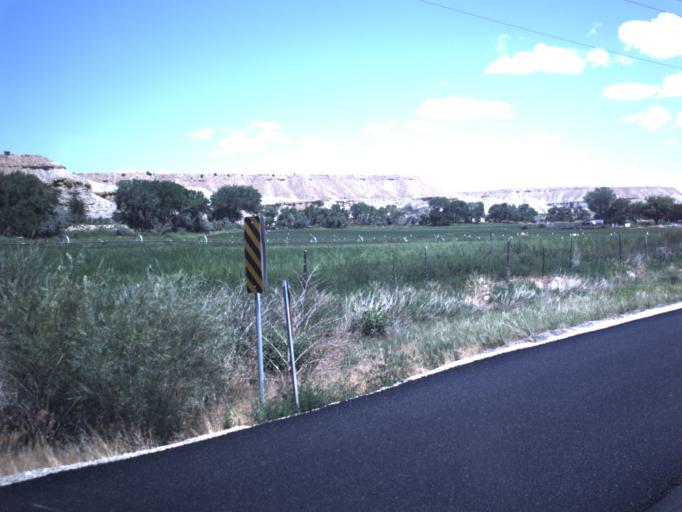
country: US
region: Utah
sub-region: Emery County
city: Orangeville
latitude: 39.2495
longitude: -111.0787
